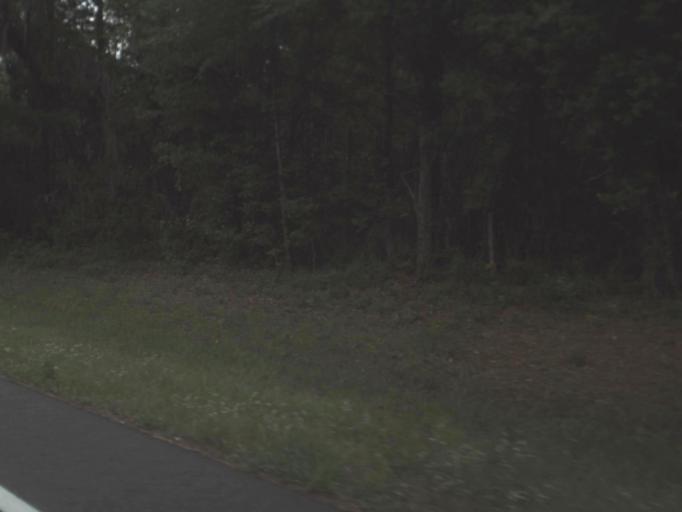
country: US
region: Florida
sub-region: Columbia County
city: Five Points
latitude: 30.4636
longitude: -82.6531
